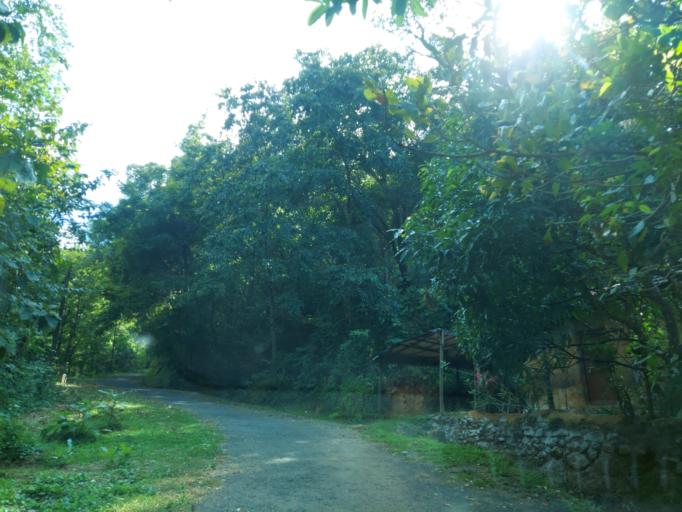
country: IN
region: Maharashtra
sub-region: Sindhudurg
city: Savantvadi
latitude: 15.9046
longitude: 73.8131
